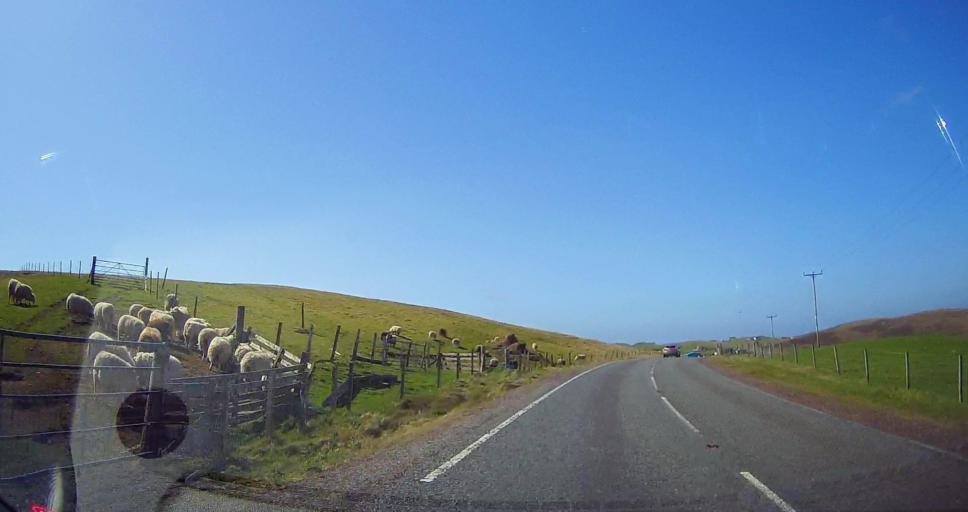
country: GB
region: Scotland
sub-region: Shetland Islands
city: Sandwick
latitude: 60.1069
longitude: -1.2990
